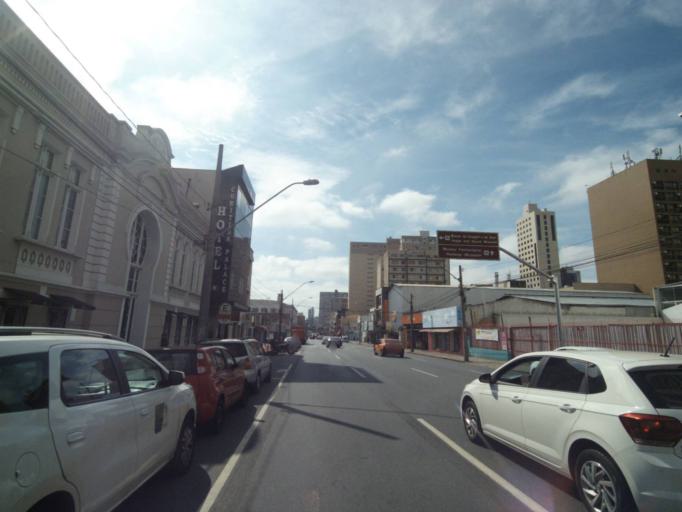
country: BR
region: Parana
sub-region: Curitiba
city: Curitiba
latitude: -25.4347
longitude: -49.2685
